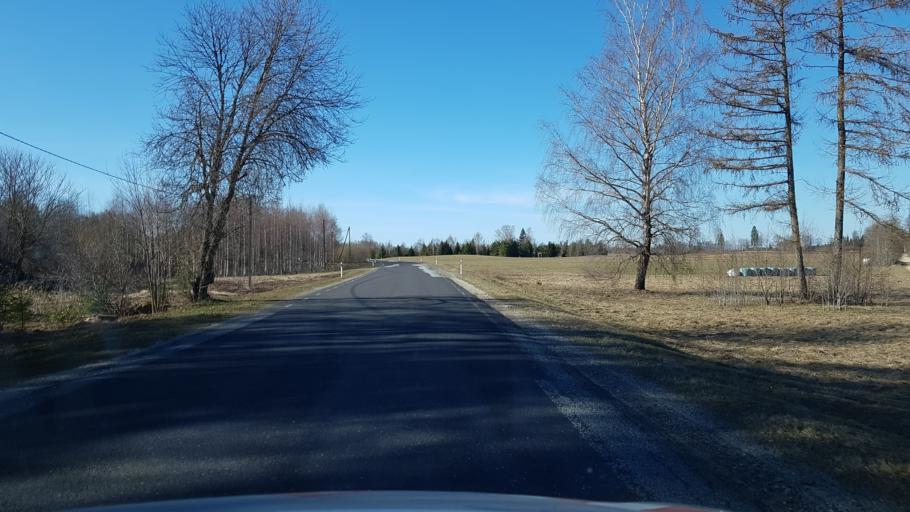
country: EE
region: Laeaene-Virumaa
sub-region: Vinni vald
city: Vinni
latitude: 59.3054
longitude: 26.5317
